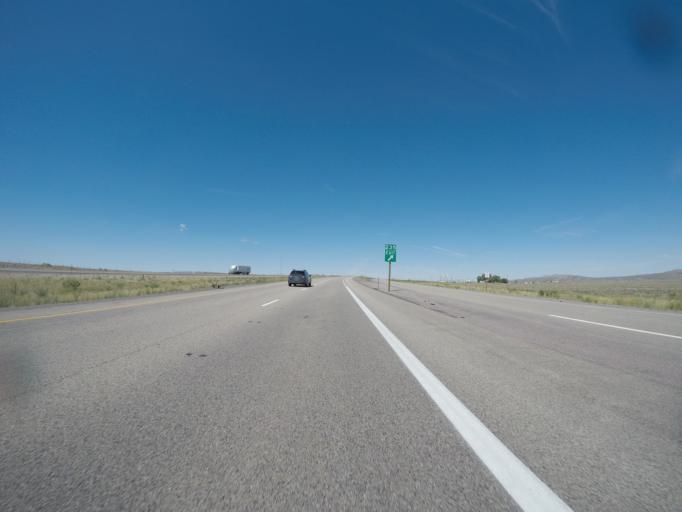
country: US
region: Wyoming
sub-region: Carbon County
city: Saratoga
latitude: 41.7414
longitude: -106.8241
